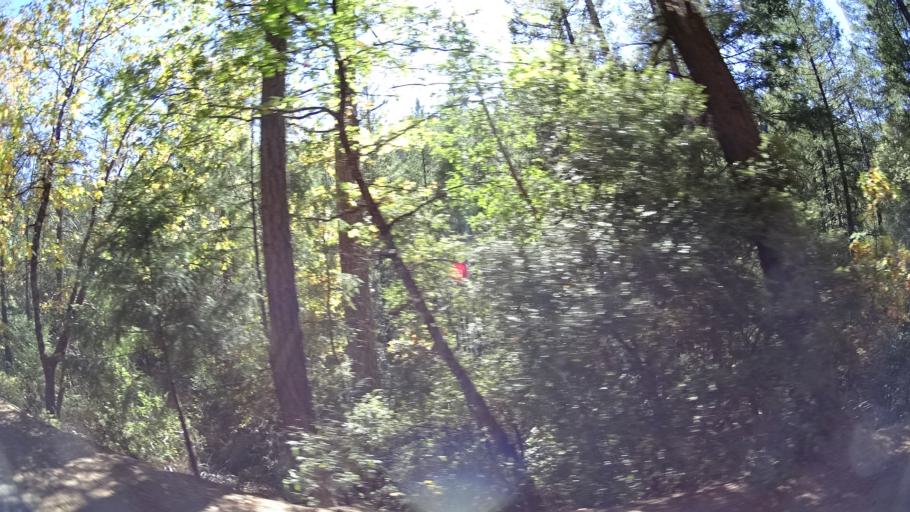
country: US
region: California
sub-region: Siskiyou County
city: Happy Camp
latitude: 41.3006
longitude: -123.1437
